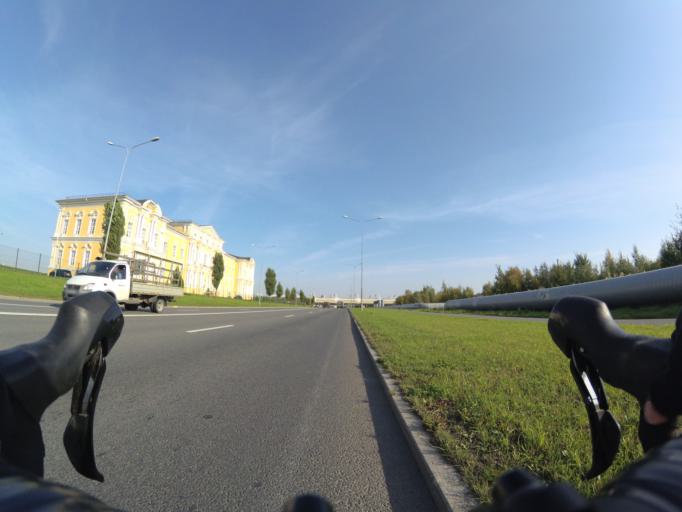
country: RU
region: St.-Petersburg
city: Staraya Derevnya
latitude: 59.9930
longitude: 30.2259
